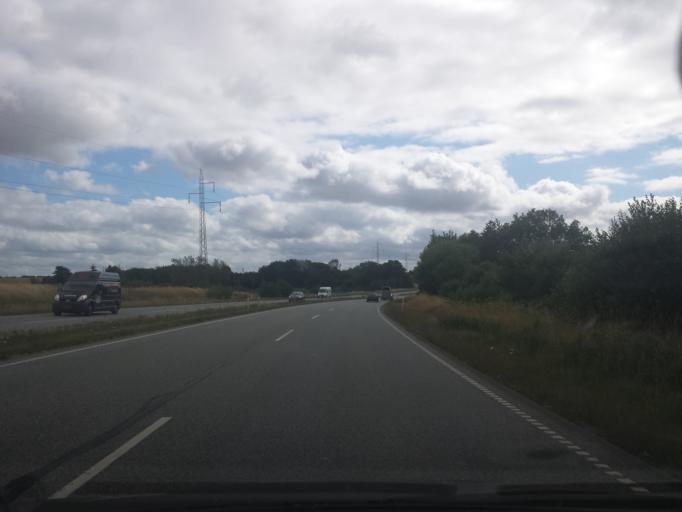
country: DK
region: South Denmark
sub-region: Sonderborg Kommune
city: Augustenborg
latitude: 54.9493
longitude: 9.8974
